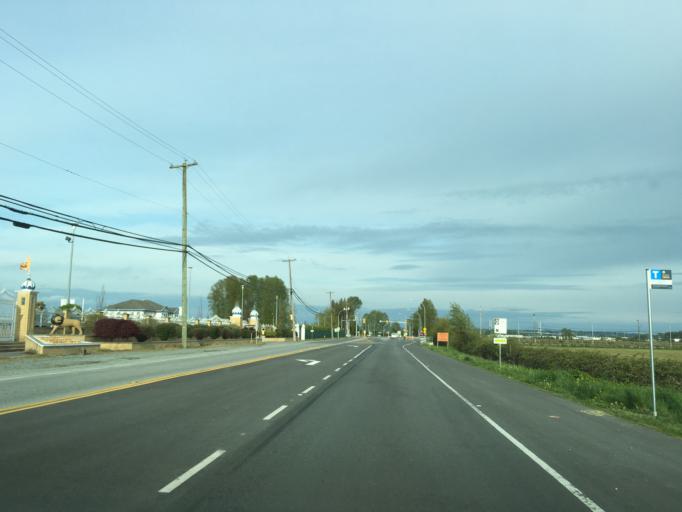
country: CA
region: British Columbia
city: Ladner
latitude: 49.1699
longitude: -123.0165
